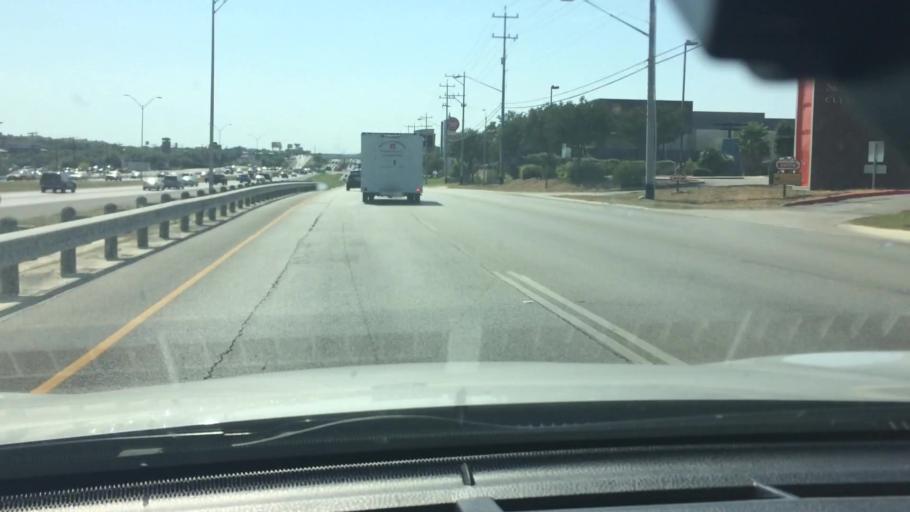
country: US
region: Texas
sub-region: Bexar County
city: Hollywood Park
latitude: 29.6092
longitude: -98.4972
